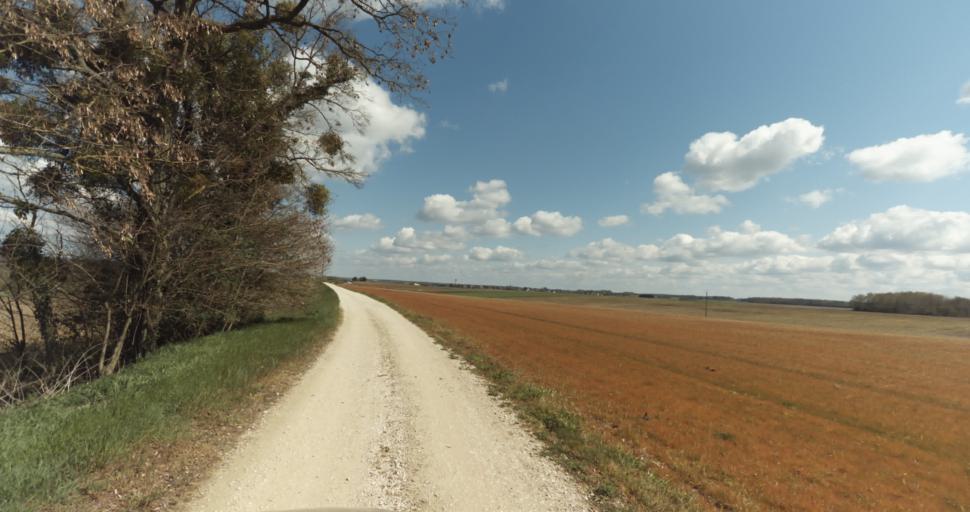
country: FR
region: Bourgogne
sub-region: Departement de la Cote-d'Or
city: Auxonne
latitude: 47.2185
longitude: 5.4210
